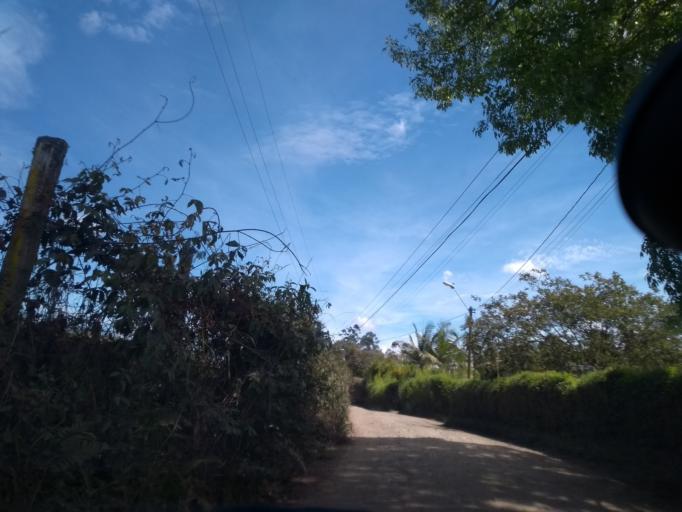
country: CO
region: Antioquia
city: Rionegro
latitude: 6.1092
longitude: -75.3942
